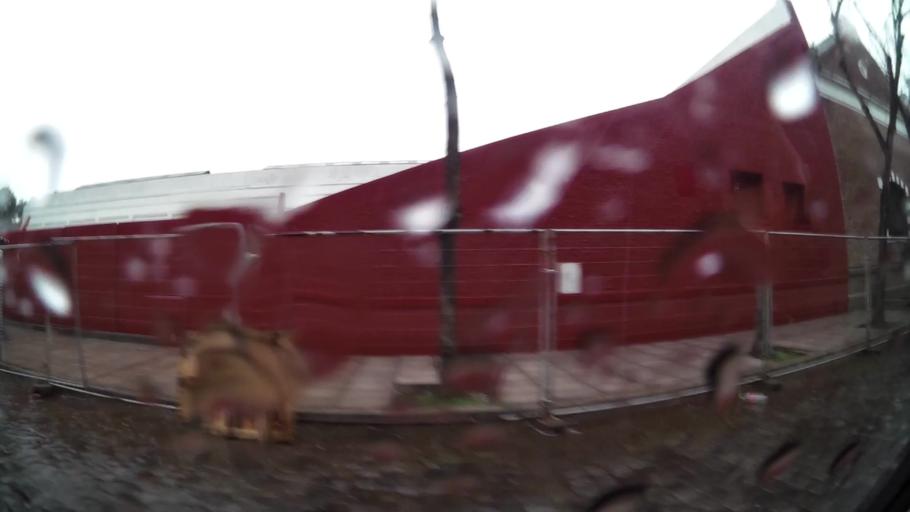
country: AR
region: Buenos Aires
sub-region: Partido de Avellaneda
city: Avellaneda
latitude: -34.6438
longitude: -58.3713
